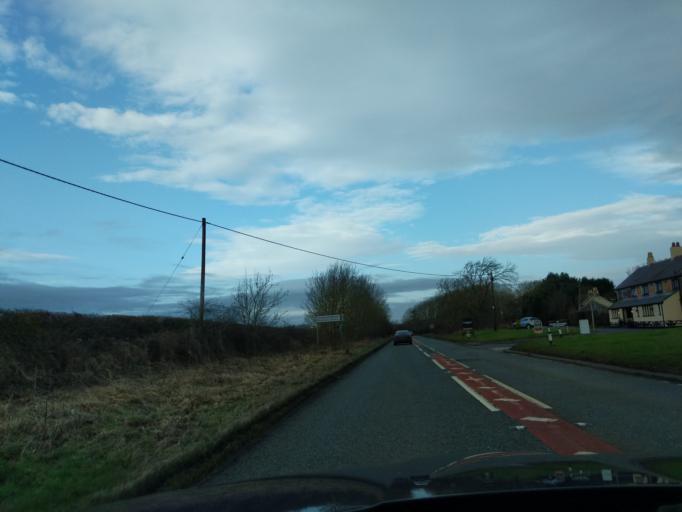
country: GB
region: England
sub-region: Northumberland
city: Darras Hall
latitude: 55.0758
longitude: -1.7985
